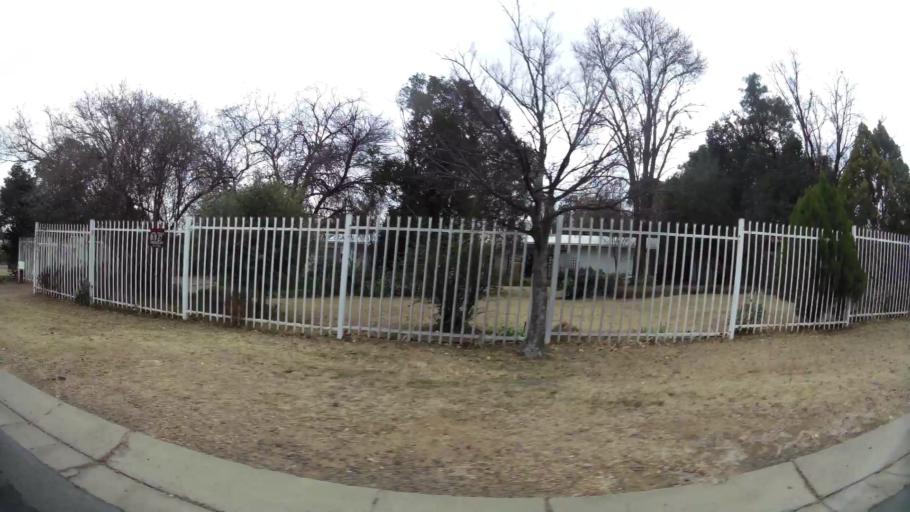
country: ZA
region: Orange Free State
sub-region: Fezile Dabi District Municipality
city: Kroonstad
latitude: -27.6840
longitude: 27.2335
